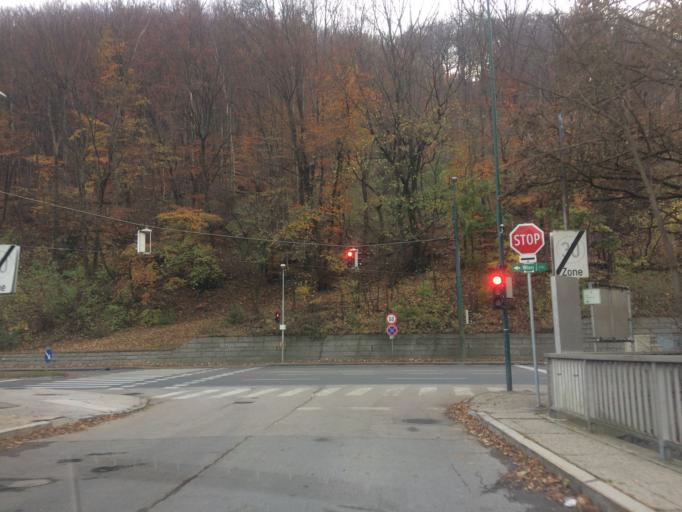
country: AT
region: Lower Austria
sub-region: Politischer Bezirk Wien-Umgebung
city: Purkersdorf
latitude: 48.2065
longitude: 16.1885
